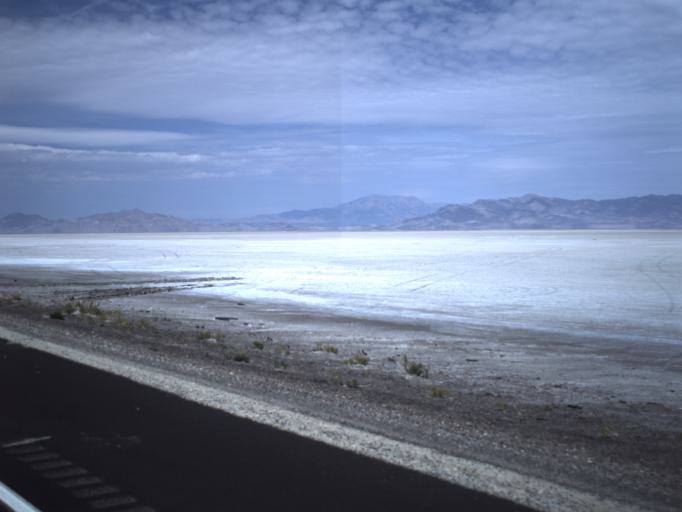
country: US
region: Utah
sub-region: Tooele County
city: Wendover
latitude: 40.7350
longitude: -113.6407
